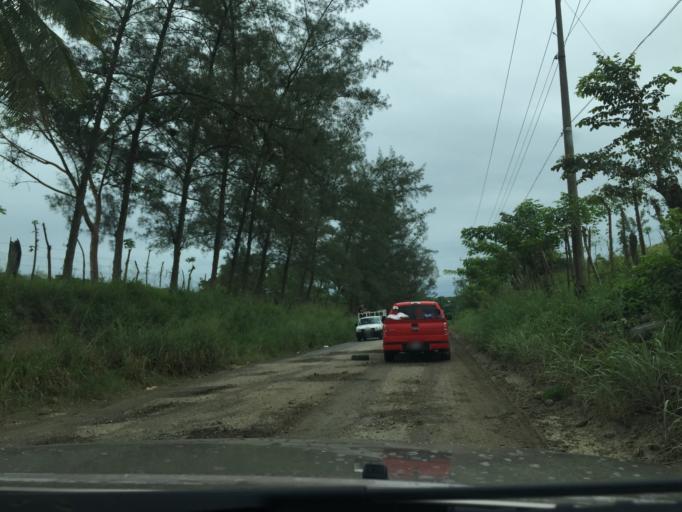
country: MX
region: Veracruz
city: Coatzintla
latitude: 20.4472
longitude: -97.4077
